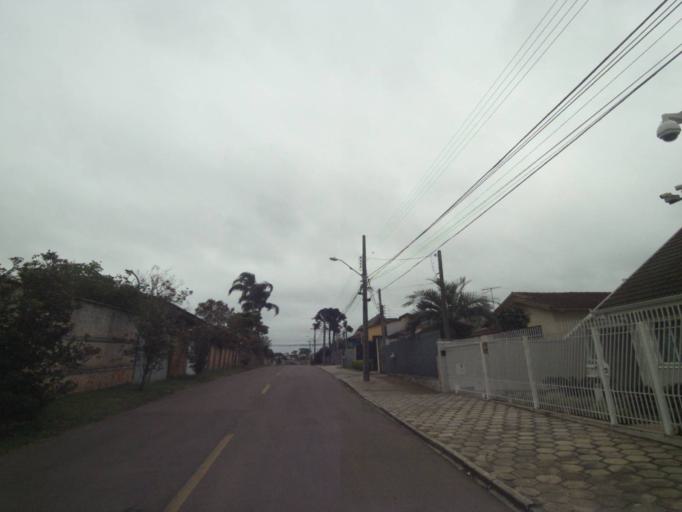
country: BR
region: Parana
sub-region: Pinhais
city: Pinhais
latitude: -25.4778
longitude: -49.2289
